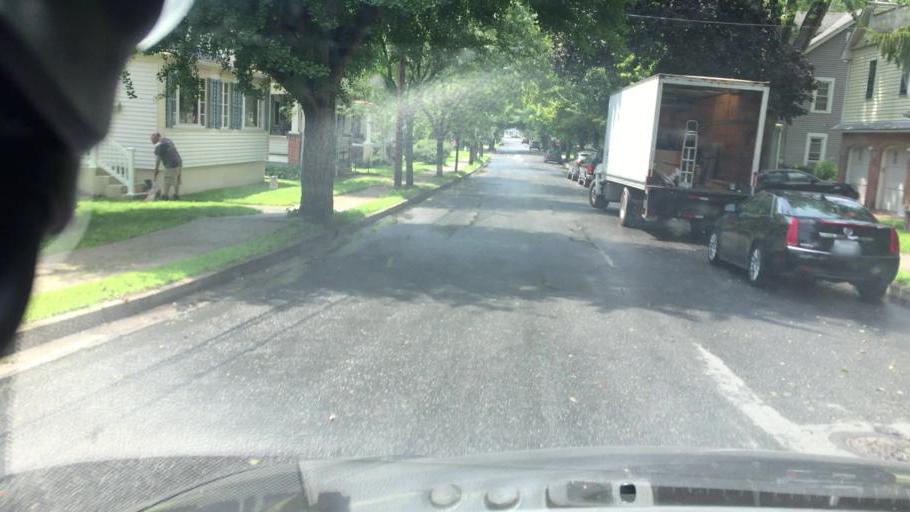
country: US
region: Pennsylvania
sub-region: Monroe County
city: Stroudsburg
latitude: 40.9885
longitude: -75.1983
